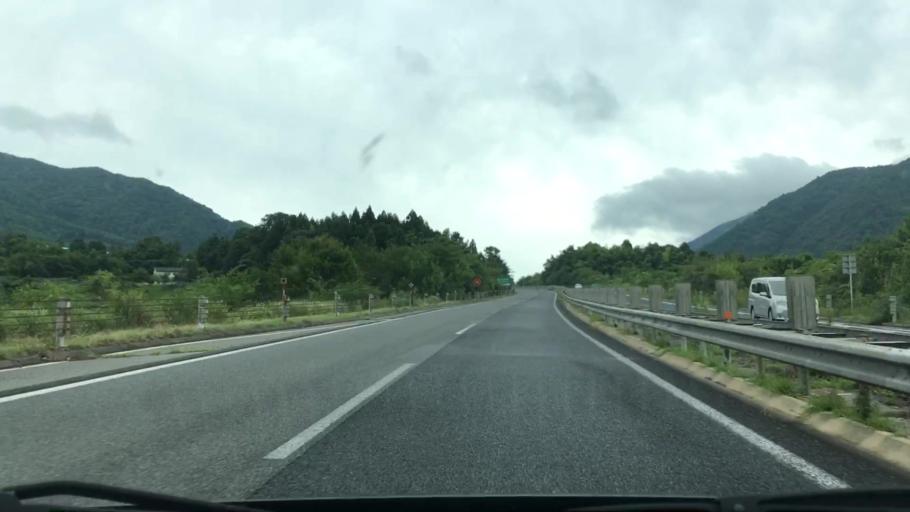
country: JP
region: Hiroshima
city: Hiroshima-shi
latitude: 34.6412
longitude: 132.5163
